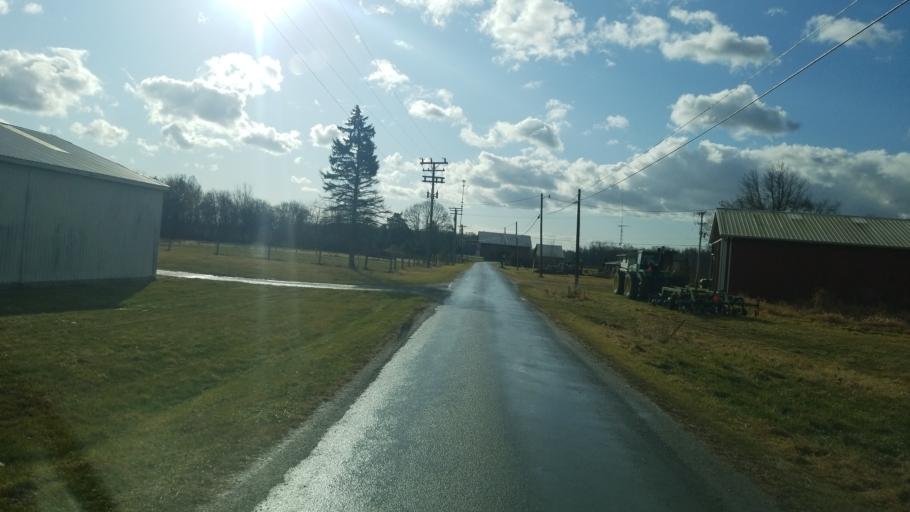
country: US
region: Ohio
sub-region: Marion County
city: Marion
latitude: 40.5359
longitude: -83.0710
